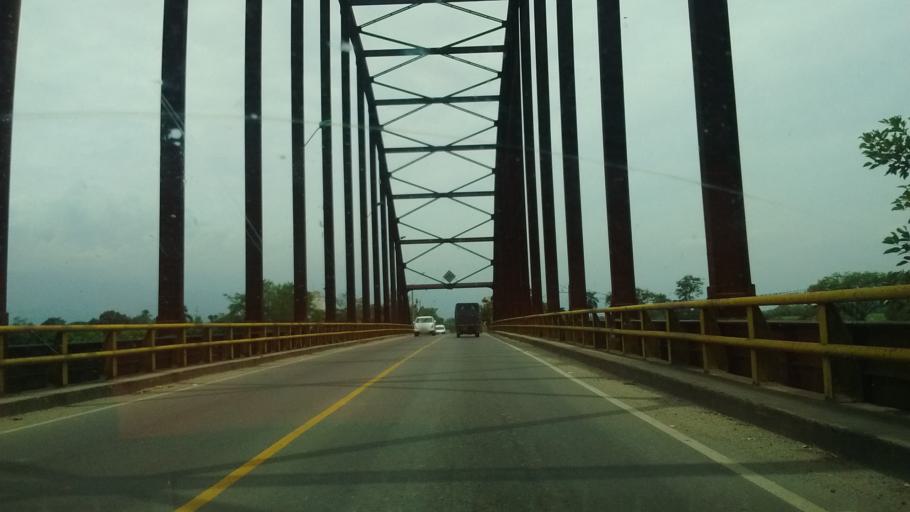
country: CO
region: Valle del Cauca
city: Jamundi
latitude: 3.3014
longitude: -76.4767
